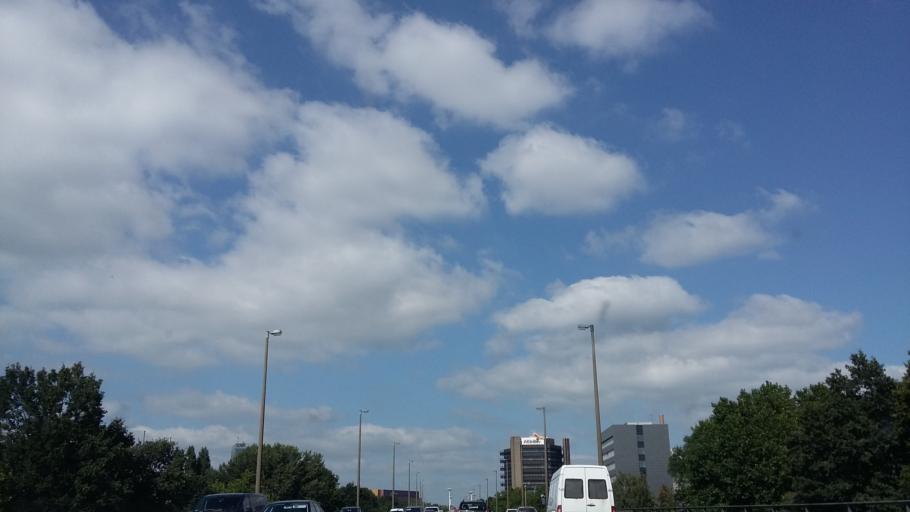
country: DE
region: Bremen
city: Bremen
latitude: 53.0742
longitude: 8.7865
